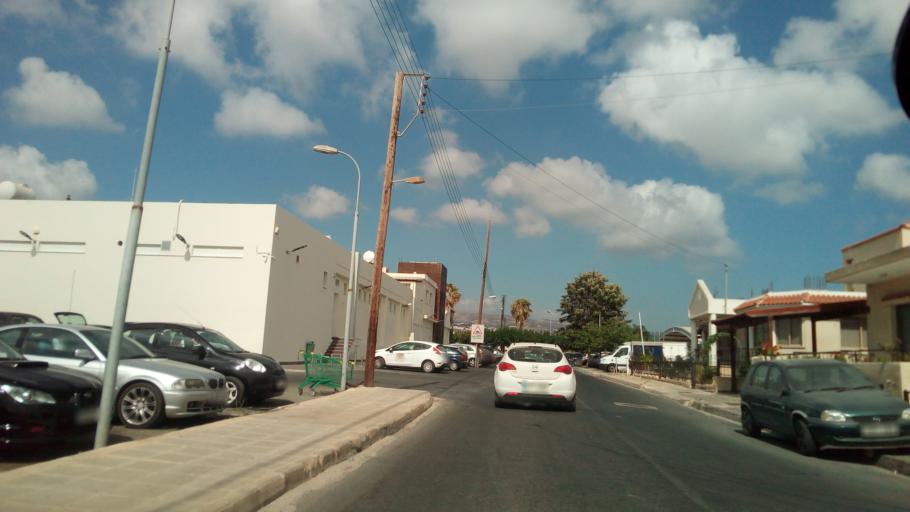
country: CY
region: Pafos
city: Chlorakas
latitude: 34.8038
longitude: 32.4096
